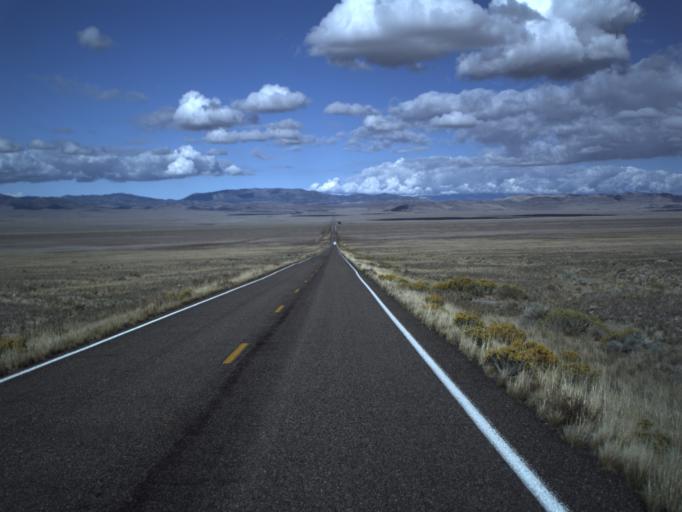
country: US
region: Utah
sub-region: Beaver County
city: Milford
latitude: 38.5139
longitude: -113.6321
